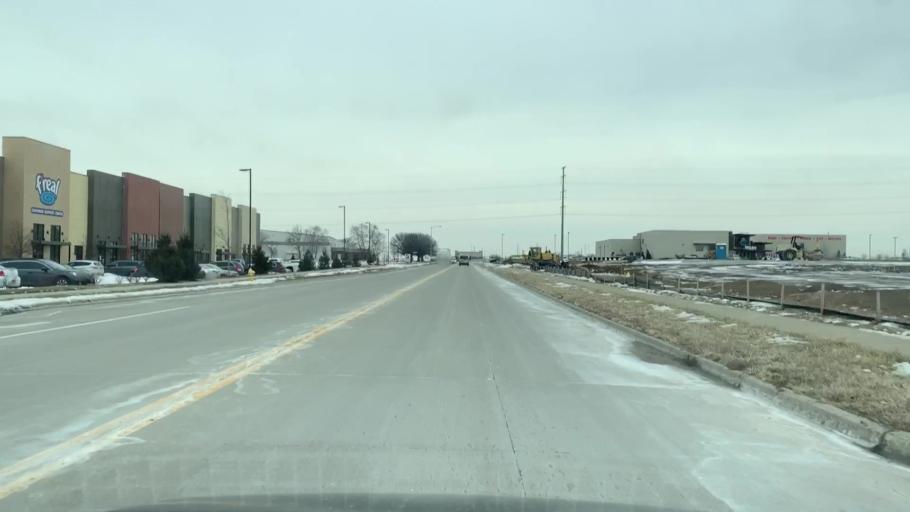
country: US
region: Missouri
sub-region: Jackson County
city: Lees Summit
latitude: 38.9628
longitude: -94.3618
